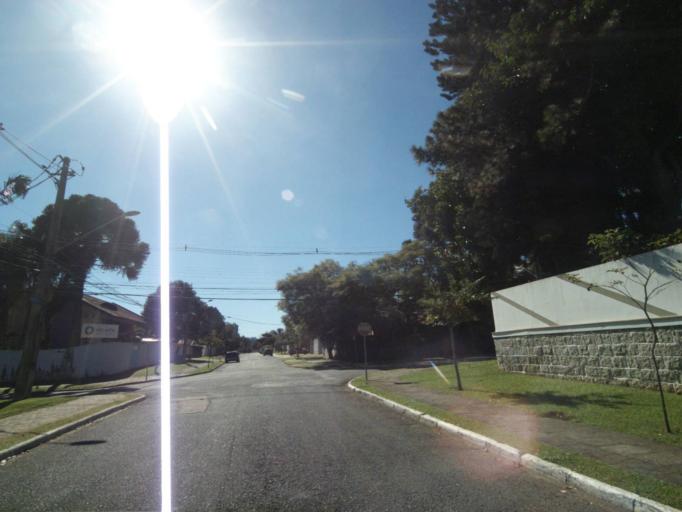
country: BR
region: Parana
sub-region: Curitiba
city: Curitiba
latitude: -25.4203
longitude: -49.2470
